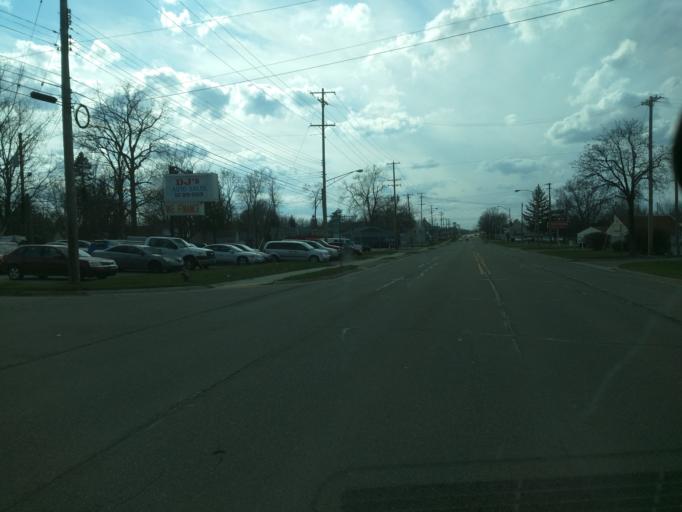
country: US
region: Michigan
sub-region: Ingham County
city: Edgemont Park
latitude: 42.7674
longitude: -84.5933
